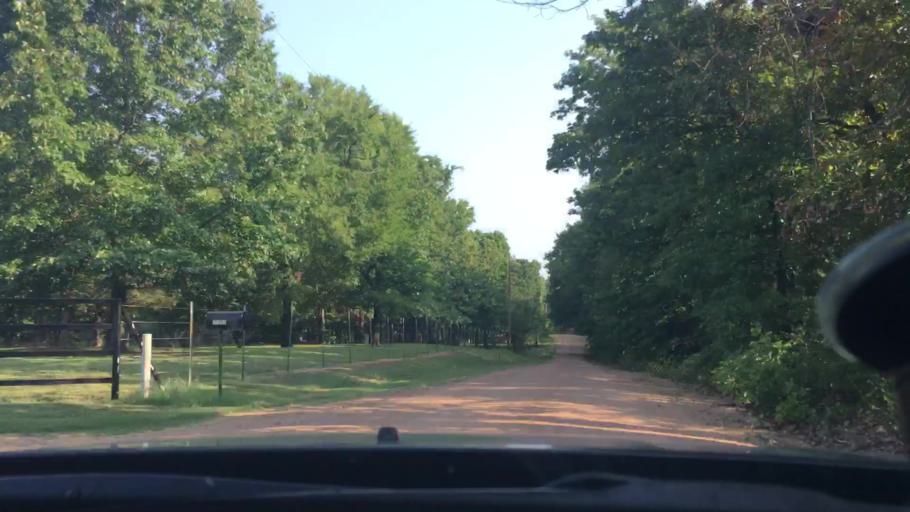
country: US
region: Oklahoma
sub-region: Johnston County
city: Tishomingo
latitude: 34.2095
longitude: -96.6186
